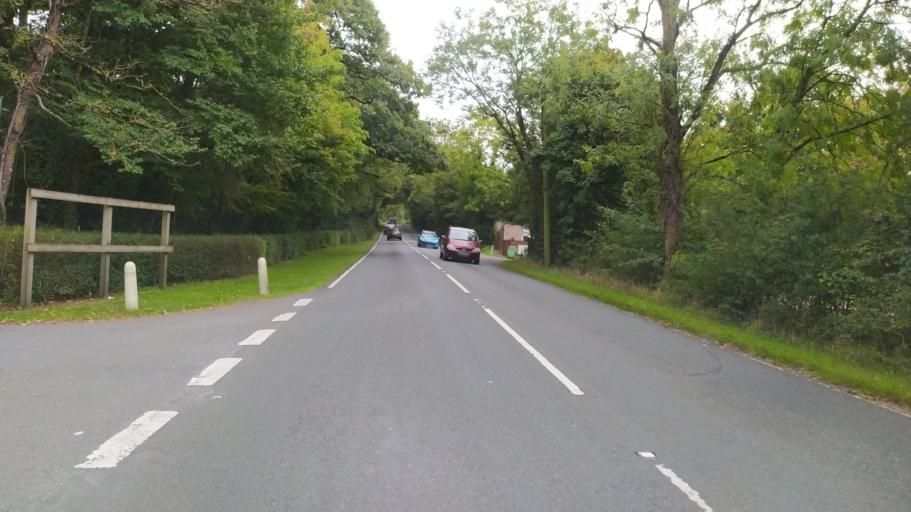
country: GB
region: England
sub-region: Dorset
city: Shaftesbury
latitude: 51.0154
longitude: -2.2154
